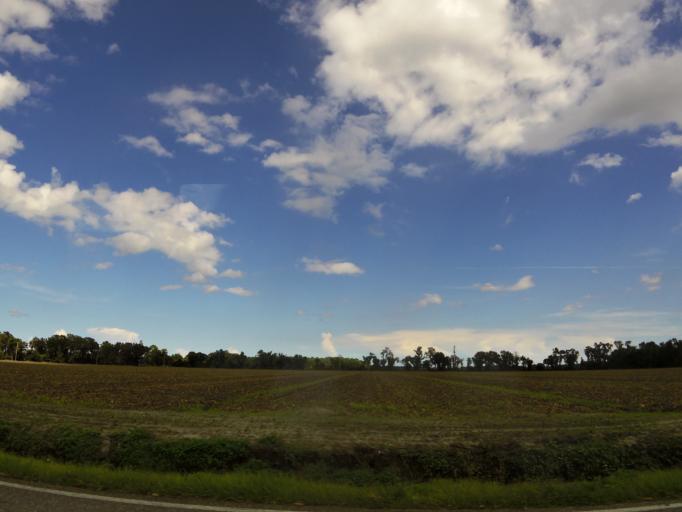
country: US
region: Florida
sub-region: Saint Johns County
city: Saint Augustine Shores
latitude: 29.7963
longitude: -81.4843
